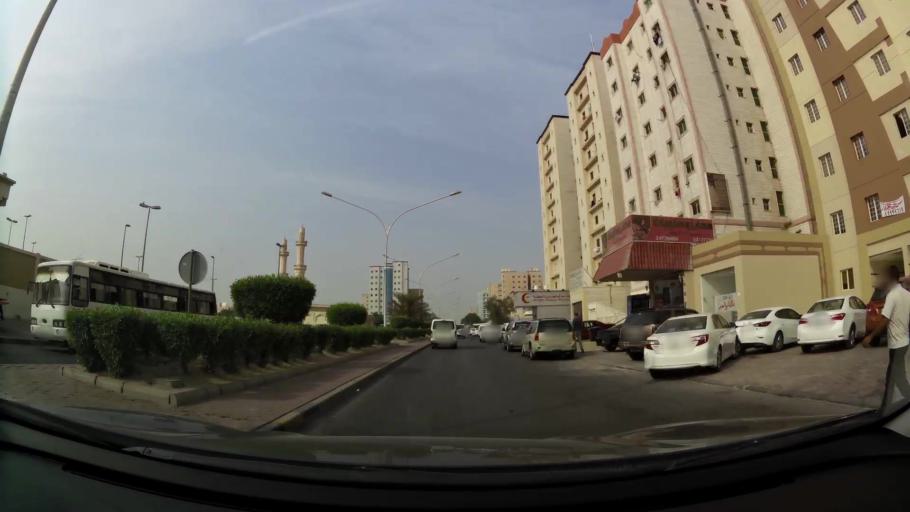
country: KW
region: Al Farwaniyah
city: Al Farwaniyah
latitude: 29.2848
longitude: 47.9553
